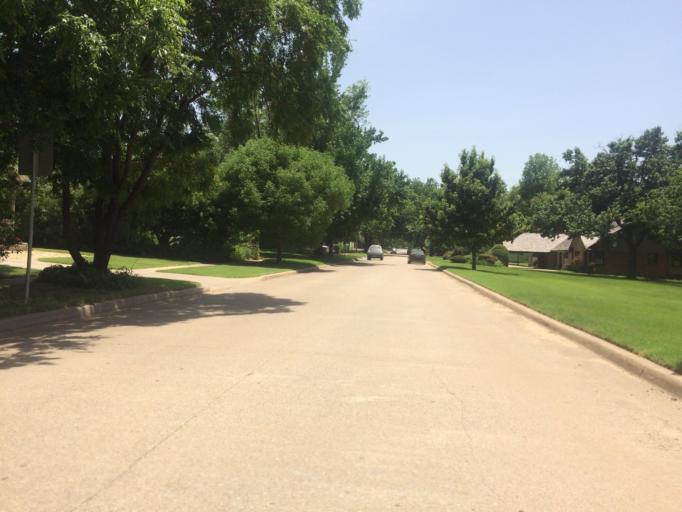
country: US
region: Oklahoma
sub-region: Cleveland County
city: Norman
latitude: 35.2104
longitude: -97.4545
